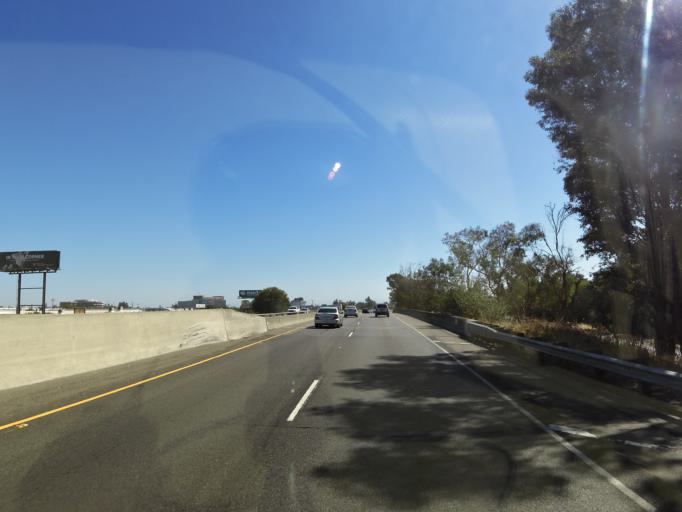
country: US
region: California
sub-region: Sacramento County
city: Sacramento
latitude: 38.5997
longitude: -121.4406
